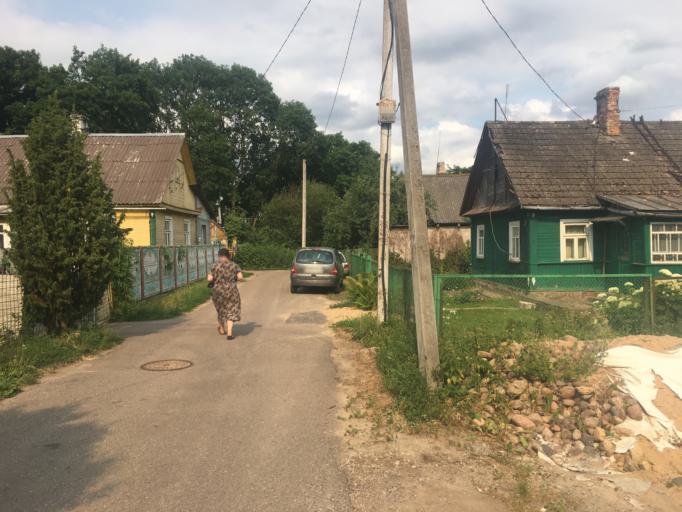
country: BY
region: Grodnenskaya
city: Hrodna
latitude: 53.6831
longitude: 23.8266
